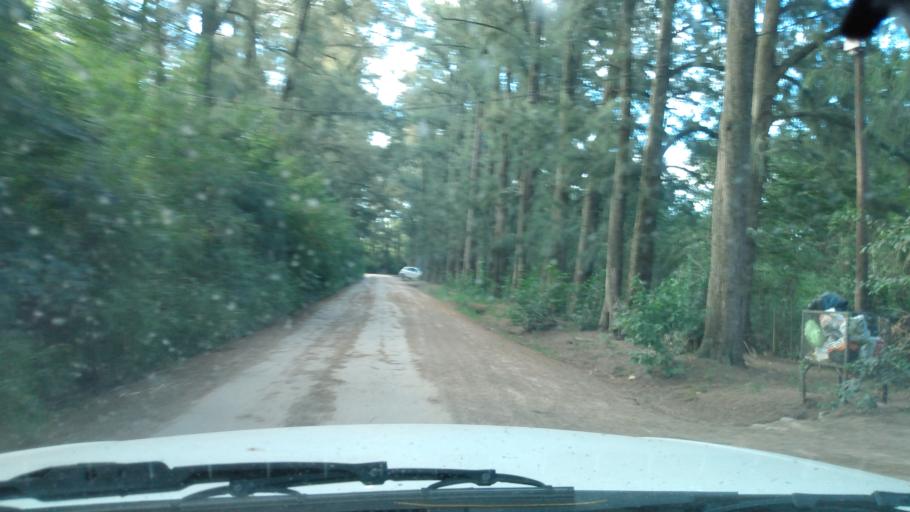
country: AR
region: Buenos Aires
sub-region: Partido de Lujan
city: Lujan
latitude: -34.5502
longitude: -59.1603
